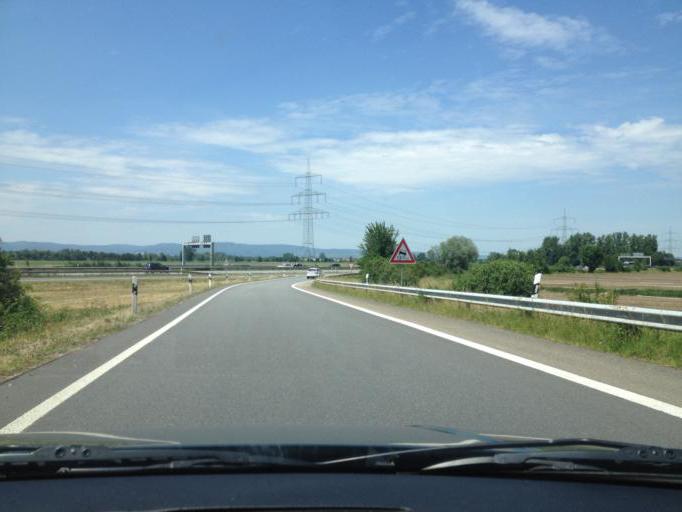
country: DE
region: Rheinland-Pfalz
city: Dannstadt-Schauernheim
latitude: 49.4445
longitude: 8.3241
